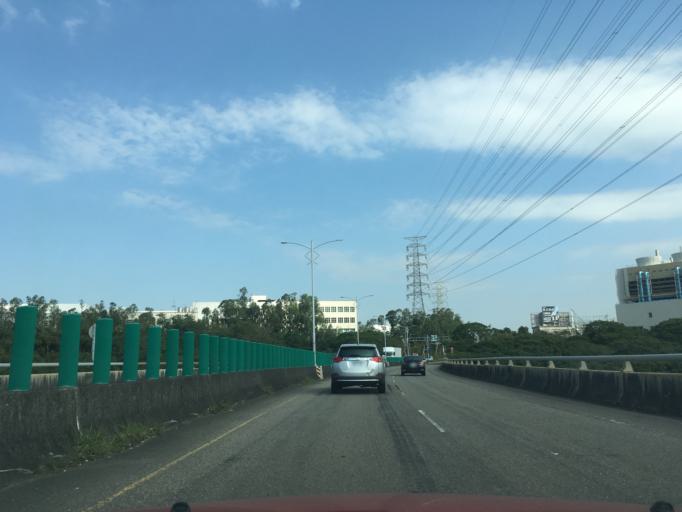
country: TW
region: Taiwan
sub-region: Hsinchu
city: Hsinchu
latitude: 24.7694
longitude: 121.0082
